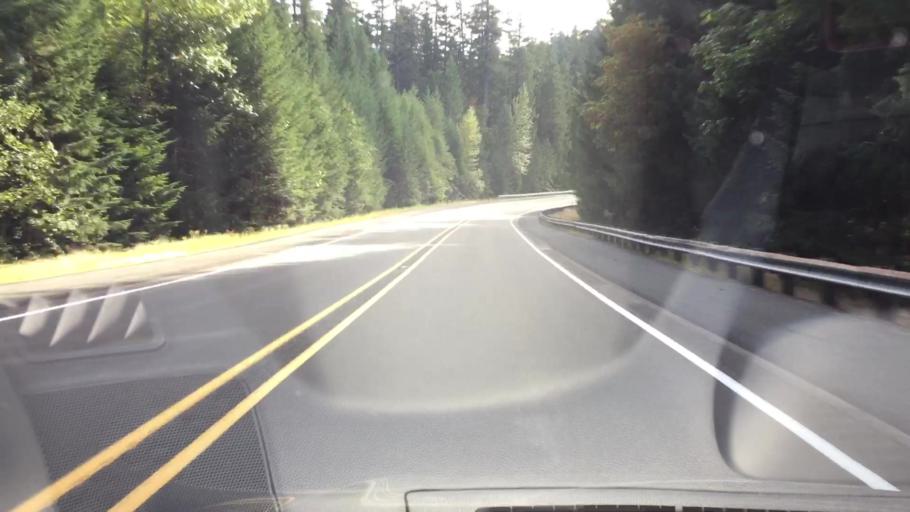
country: US
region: Washington
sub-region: Pierce County
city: Buckley
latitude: 46.6712
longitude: -121.5849
